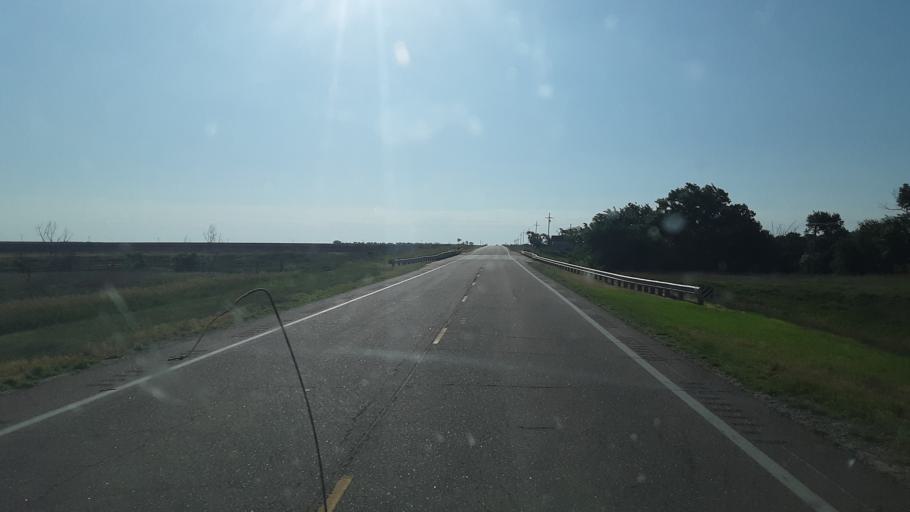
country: US
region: Kansas
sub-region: Pawnee County
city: Larned
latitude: 38.1897
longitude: -99.3247
